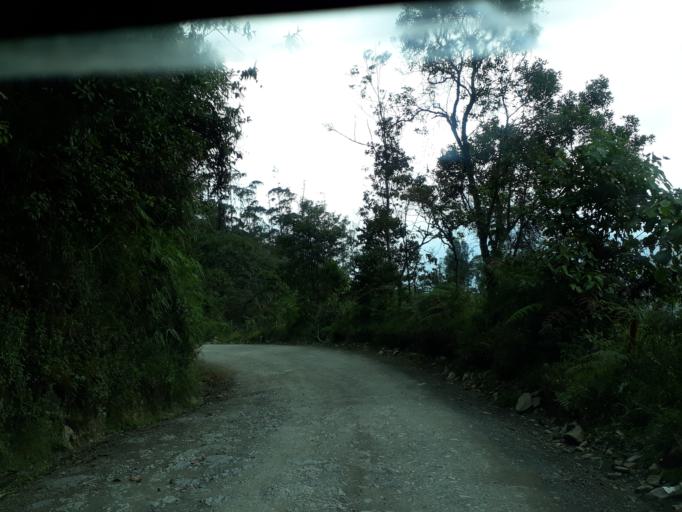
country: CO
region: Cundinamarca
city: Pacho
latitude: 5.2324
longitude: -74.1835
